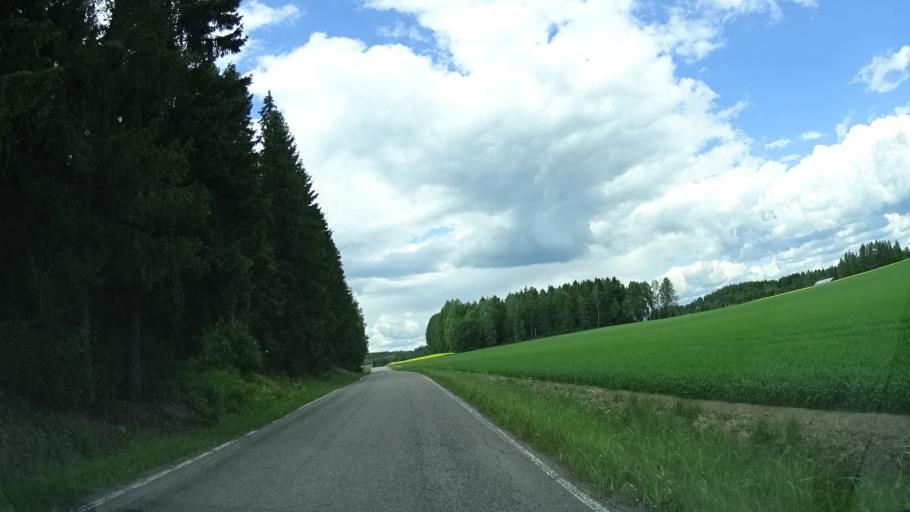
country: FI
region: Uusimaa
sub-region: Helsinki
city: Nurmijaervi
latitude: 60.4016
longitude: 24.6190
